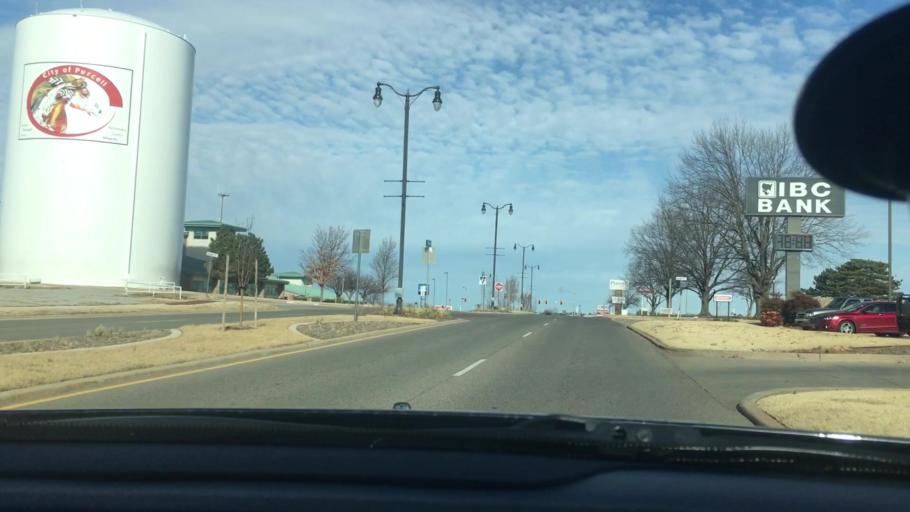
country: US
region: Oklahoma
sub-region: McClain County
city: Purcell
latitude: 35.0273
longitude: -97.3656
